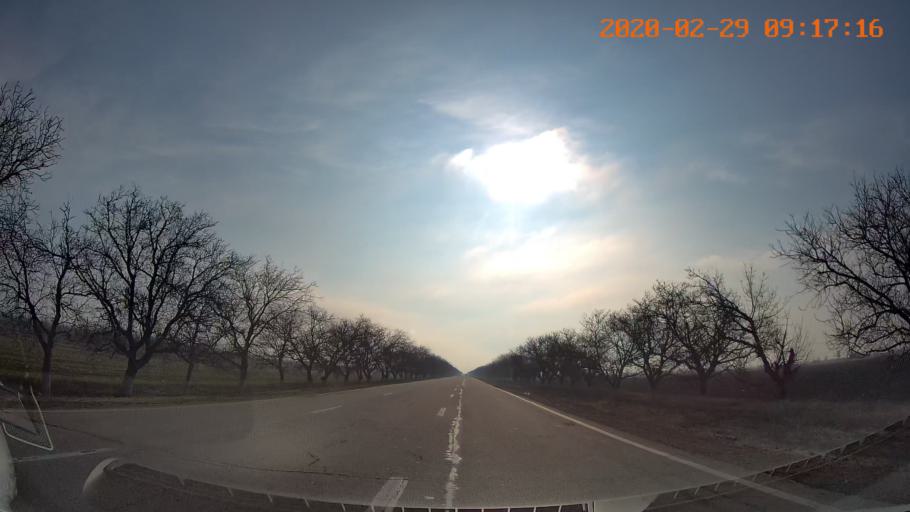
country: MD
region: Telenesti
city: Pervomaisc
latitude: 46.7846
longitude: 29.9011
